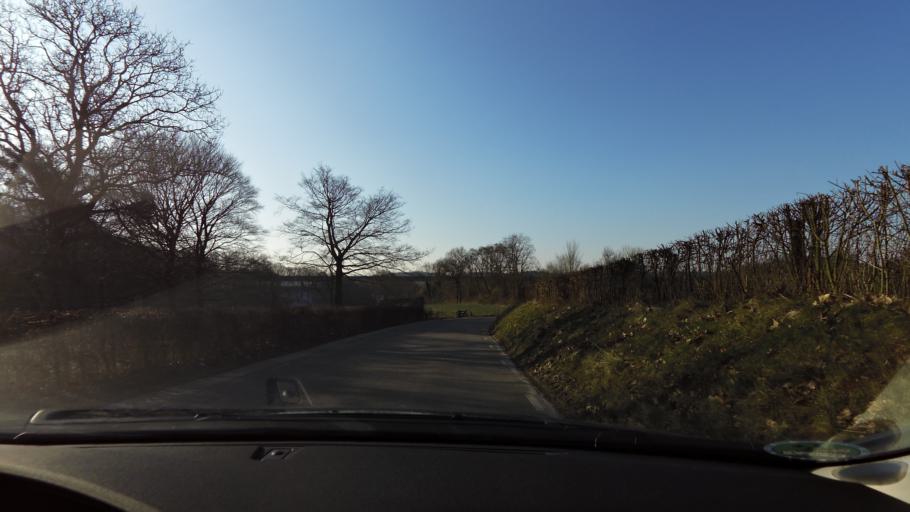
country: NL
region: Limburg
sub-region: Valkenburg aan de Geul
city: Broekhem
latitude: 50.8778
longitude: 5.8148
